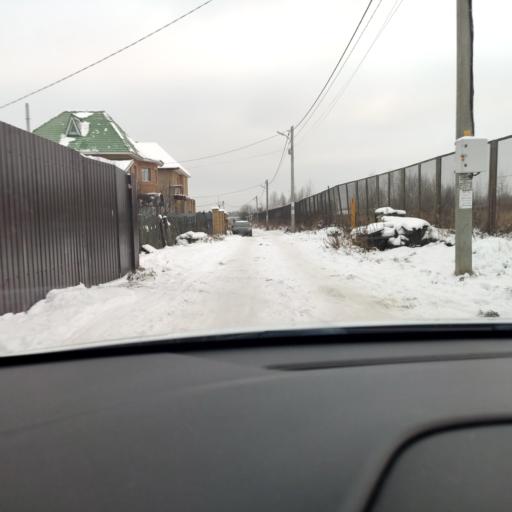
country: RU
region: Tatarstan
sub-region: Gorod Kazan'
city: Kazan
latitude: 55.8690
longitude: 49.1437
